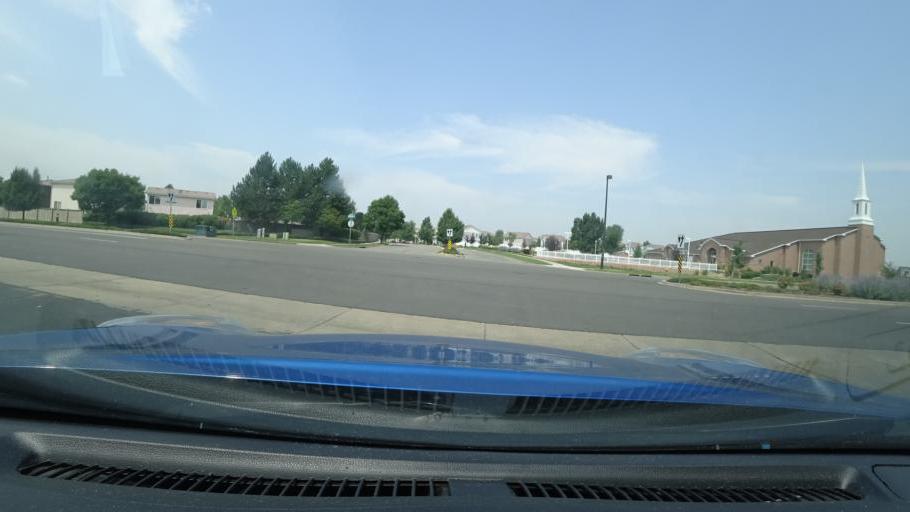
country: US
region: Colorado
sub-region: Adams County
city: Aurora
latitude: 39.7816
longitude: -104.7559
